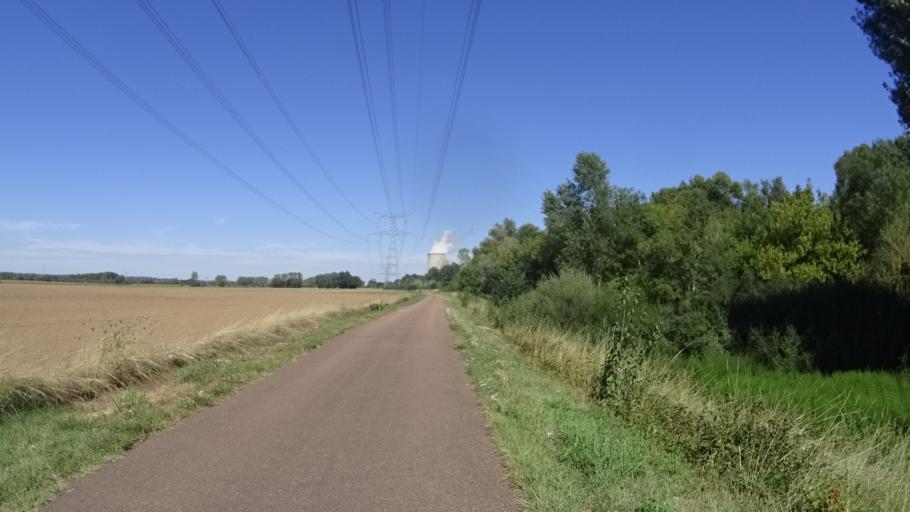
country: FR
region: Centre
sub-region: Departement du Cher
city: Lere
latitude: 47.4917
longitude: 2.8921
